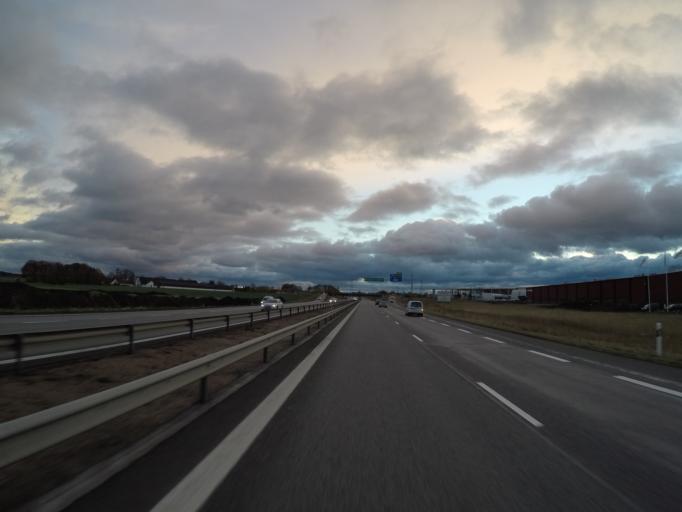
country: SE
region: Skane
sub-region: Kristianstads Kommun
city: Norra Asum
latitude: 56.0054
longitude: 14.1058
